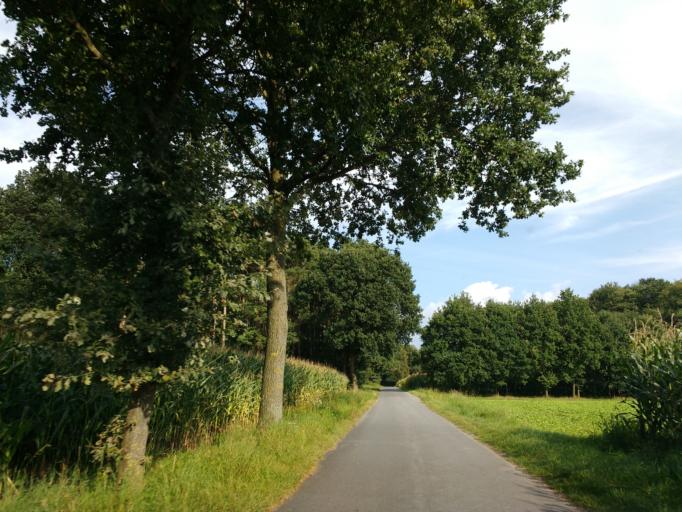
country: DE
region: North Rhine-Westphalia
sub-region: Regierungsbezirk Detmold
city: Delbruck
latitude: 51.7735
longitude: 8.6012
